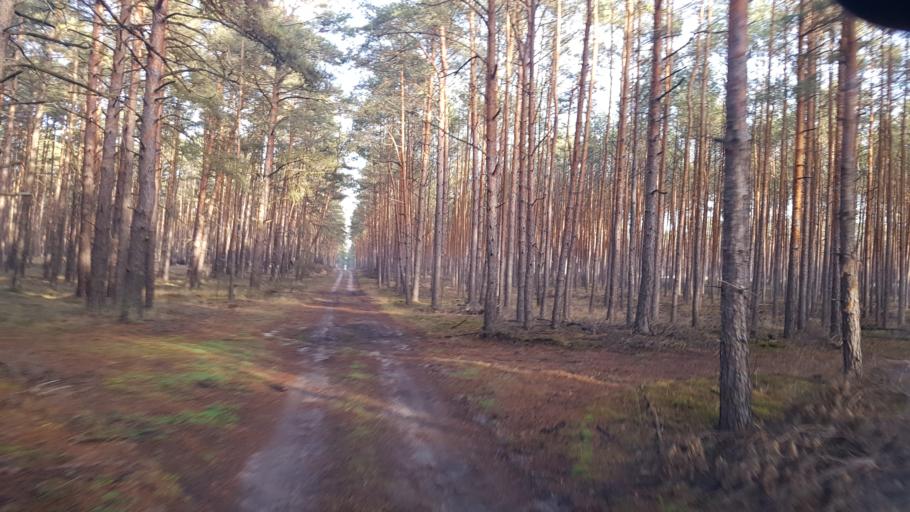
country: DE
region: Brandenburg
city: Schilda
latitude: 51.6313
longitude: 13.3950
